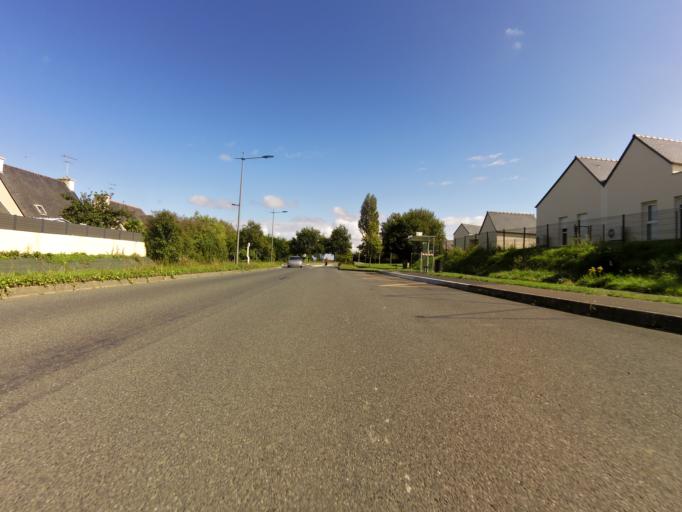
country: FR
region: Brittany
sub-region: Departement des Cotes-d'Armor
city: Langueux
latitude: 48.4852
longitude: -2.7414
